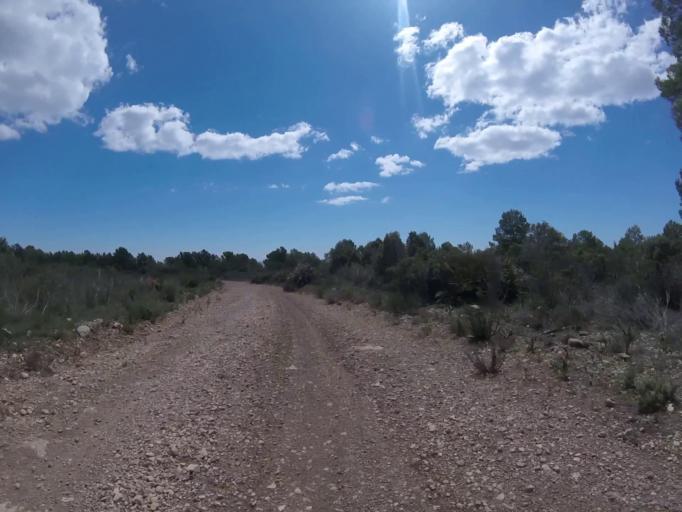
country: ES
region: Valencia
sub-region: Provincia de Castello
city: Alcoceber
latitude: 40.2860
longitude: 0.3215
